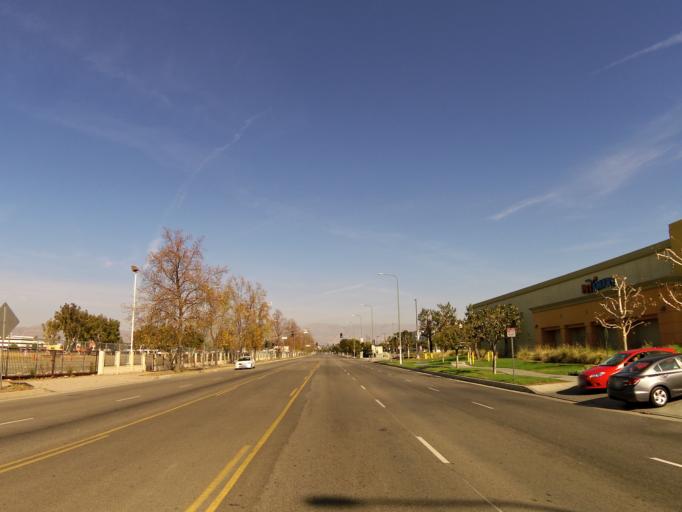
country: US
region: California
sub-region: Los Angeles County
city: Canoga Park
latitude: 34.1893
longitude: -118.5974
